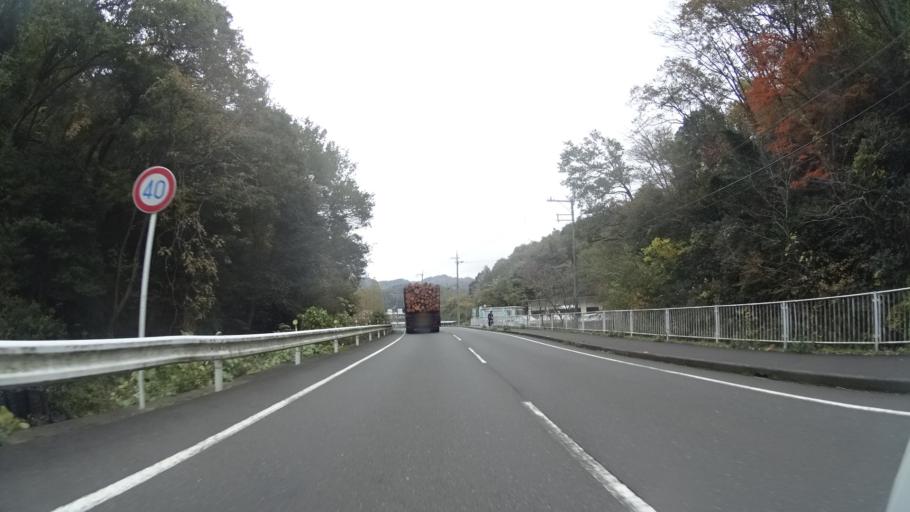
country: JP
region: Kyoto
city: Maizuru
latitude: 35.4935
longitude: 135.4370
